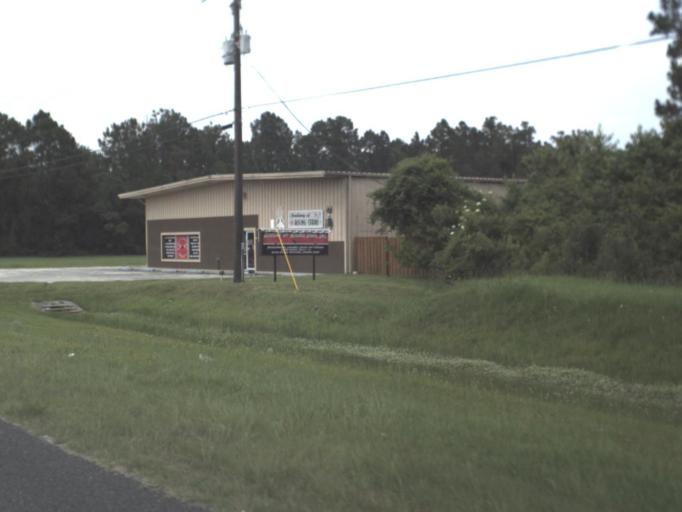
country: US
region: Florida
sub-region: Putnam County
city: Palatka
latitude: 29.6715
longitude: -81.6577
